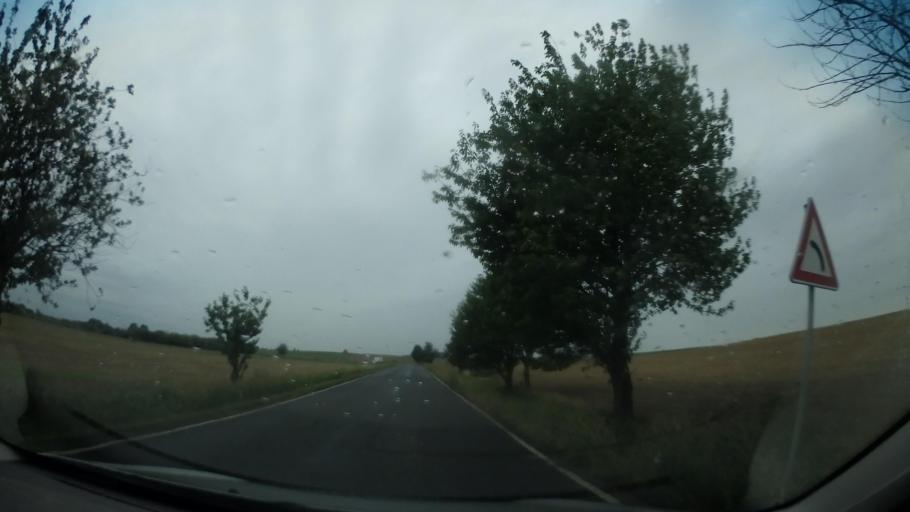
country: CZ
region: Central Bohemia
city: Loucen
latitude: 50.2525
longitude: 15.0234
